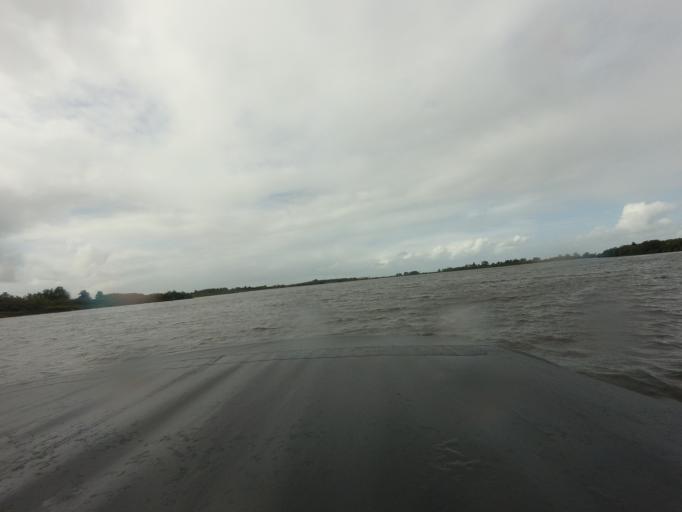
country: NL
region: Friesland
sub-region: Gemeente Boarnsterhim
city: Warten
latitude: 53.1343
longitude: 5.9024
